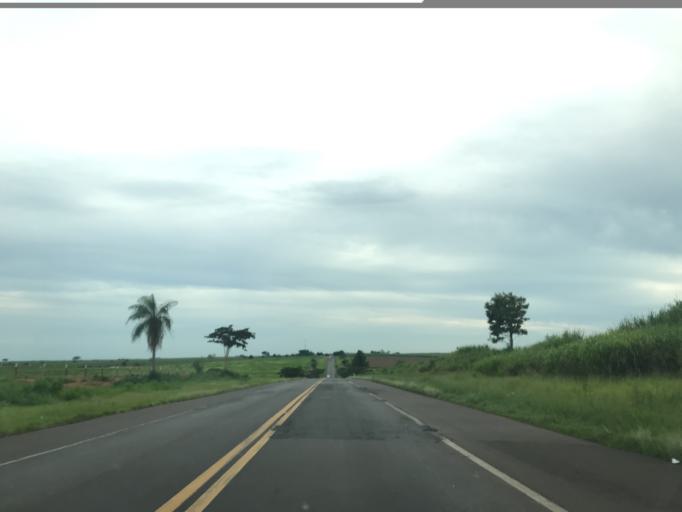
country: BR
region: Sao Paulo
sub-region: Tupa
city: Tupa
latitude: -21.6628
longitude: -50.5539
